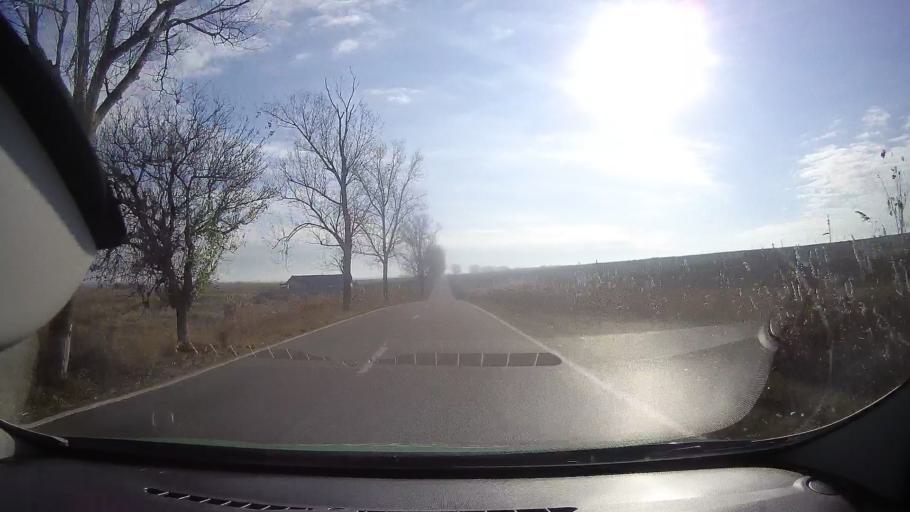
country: RO
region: Tulcea
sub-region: Comuna Mahmudia
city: Mahmudia
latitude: 45.0640
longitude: 29.1102
